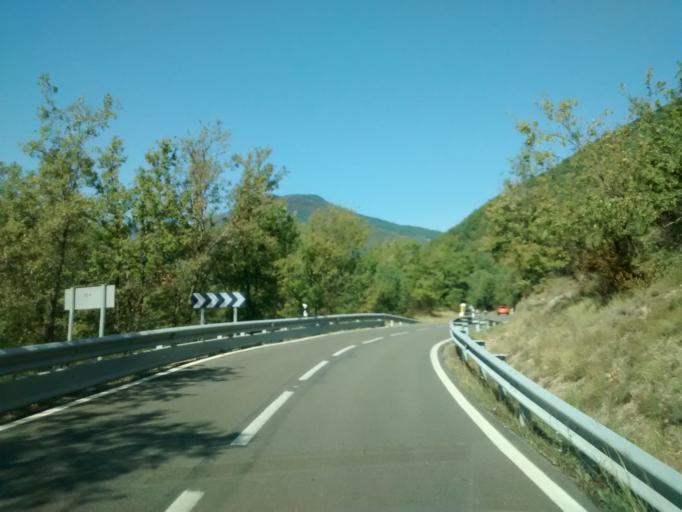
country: ES
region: Aragon
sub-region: Provincia de Huesca
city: Fiscal
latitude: 42.4937
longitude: -0.1054
